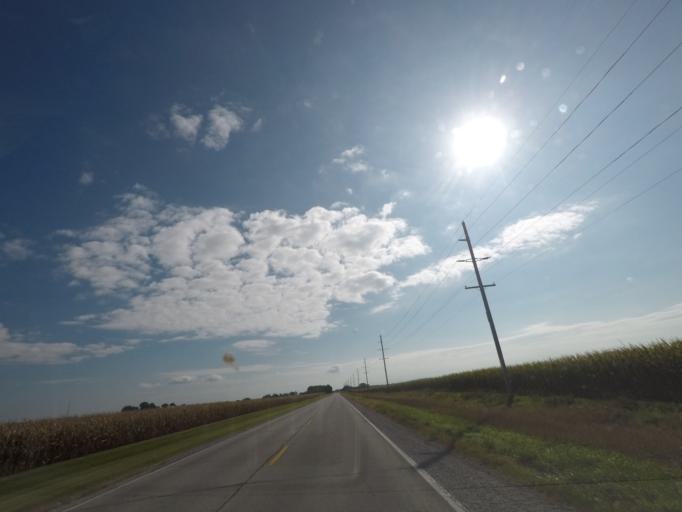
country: US
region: Iowa
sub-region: Story County
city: Nevada
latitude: 42.0227
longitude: -93.4148
